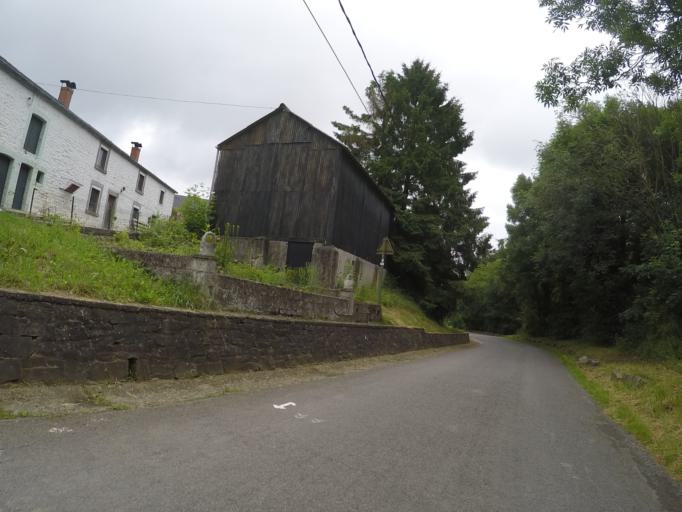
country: BE
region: Wallonia
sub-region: Province de Namur
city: Yvoir
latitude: 50.3227
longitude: 4.9105
